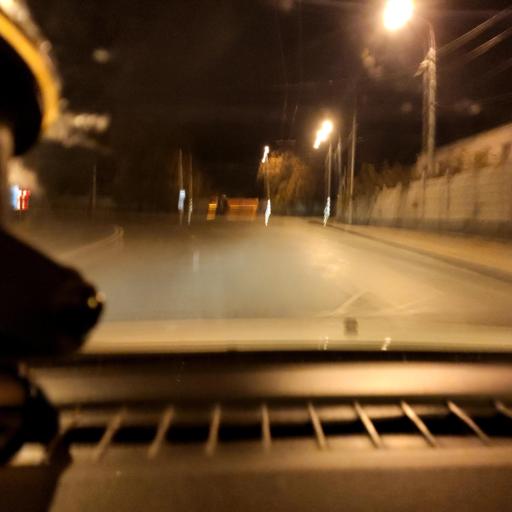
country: RU
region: Samara
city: Rozhdestveno
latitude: 53.1663
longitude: 50.0736
